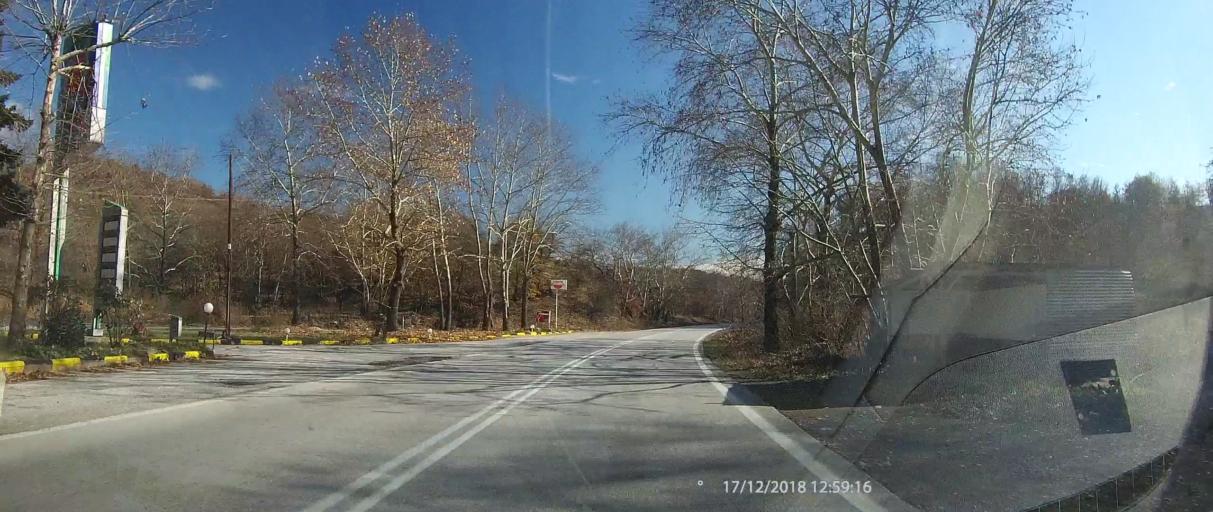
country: GR
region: Thessaly
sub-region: Trikala
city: Kastraki
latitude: 39.7383
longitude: 21.5540
